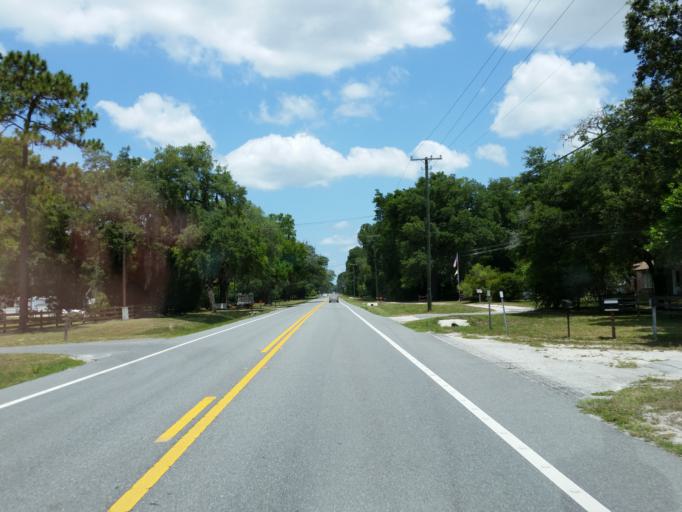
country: US
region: Florida
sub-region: Sumter County
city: Bushnell
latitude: 28.6920
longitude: -82.1042
